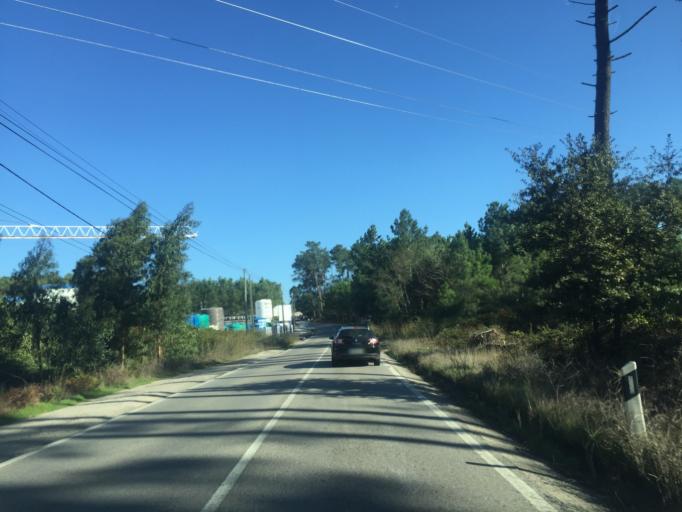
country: PT
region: Leiria
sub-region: Leiria
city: Amor
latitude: 39.8170
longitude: -8.8426
